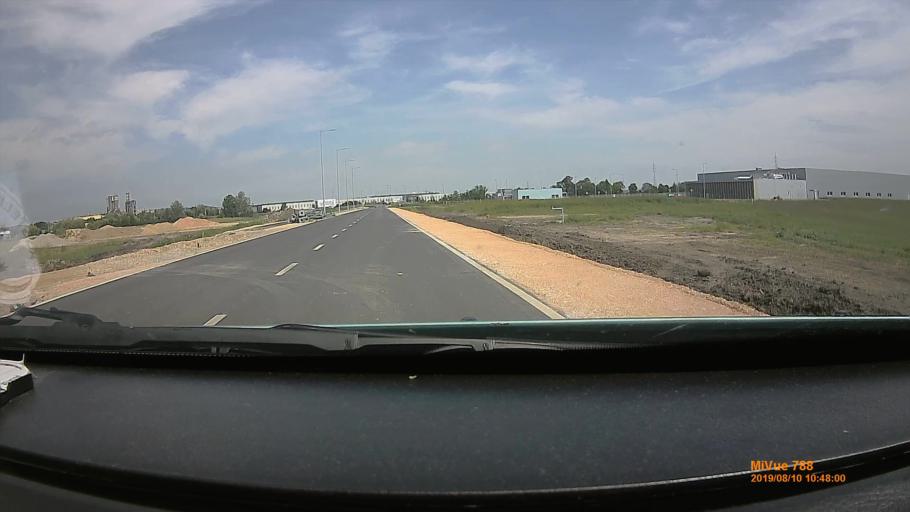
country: HU
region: Borsod-Abauj-Zemplen
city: Malyi
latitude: 48.0522
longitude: 20.8100
